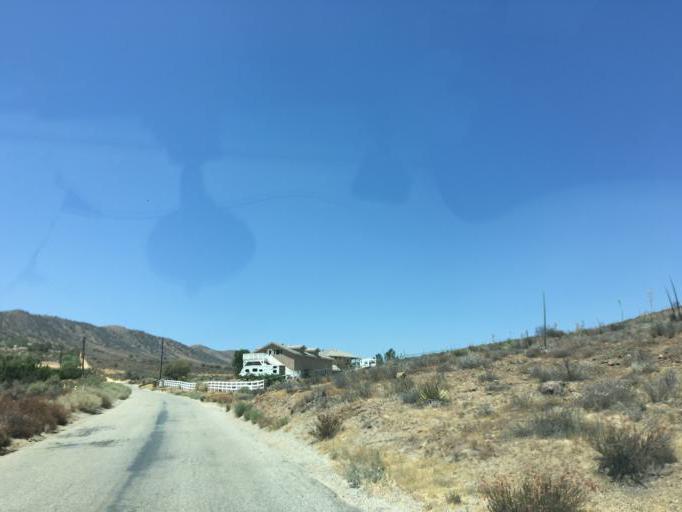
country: US
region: California
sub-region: Los Angeles County
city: Acton
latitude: 34.4732
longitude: -118.2083
